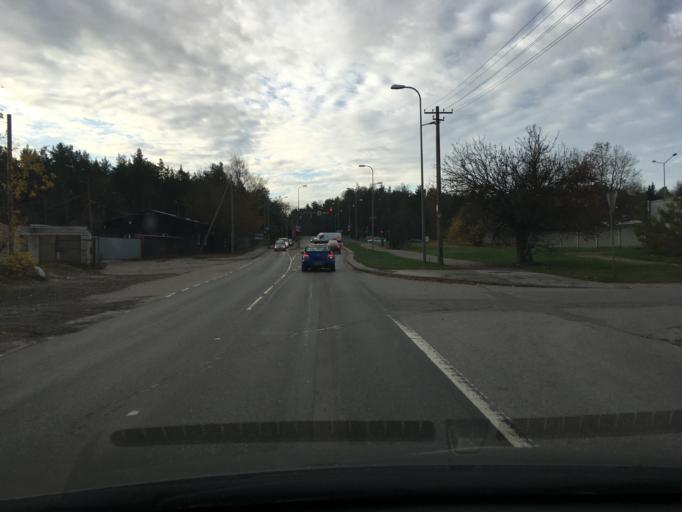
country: EE
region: Harju
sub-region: Tallinna linn
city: Tallinn
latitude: 59.3956
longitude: 24.7093
